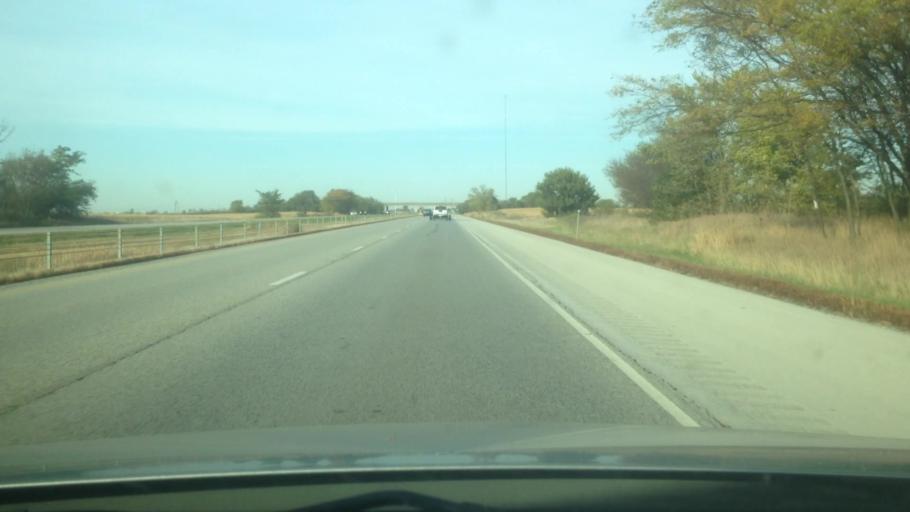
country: US
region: Illinois
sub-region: Kankakee County
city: Manteno
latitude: 41.2899
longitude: -87.8331
